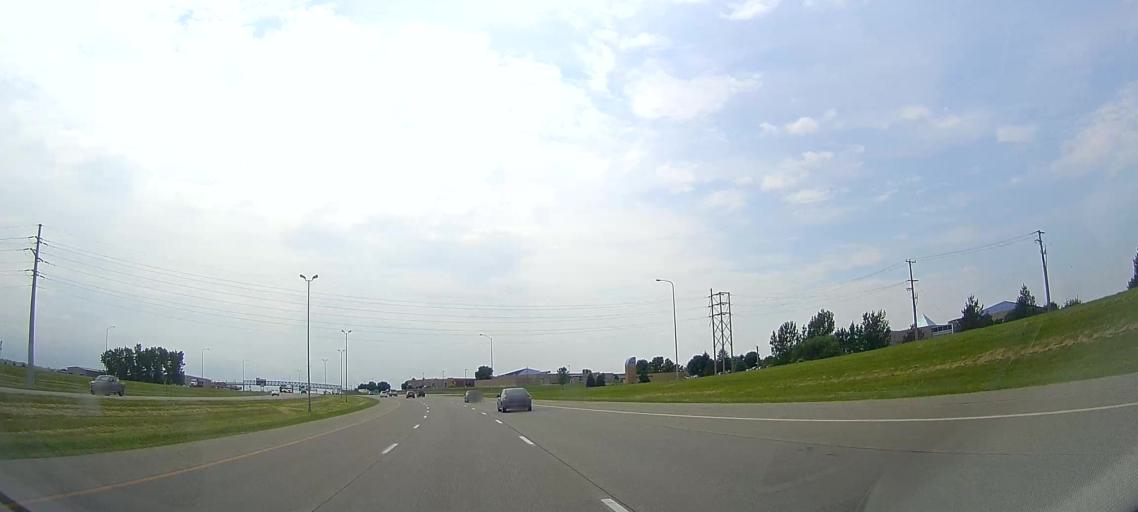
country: US
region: South Dakota
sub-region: Minnehaha County
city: Sioux Falls
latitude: 43.5698
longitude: -96.7777
